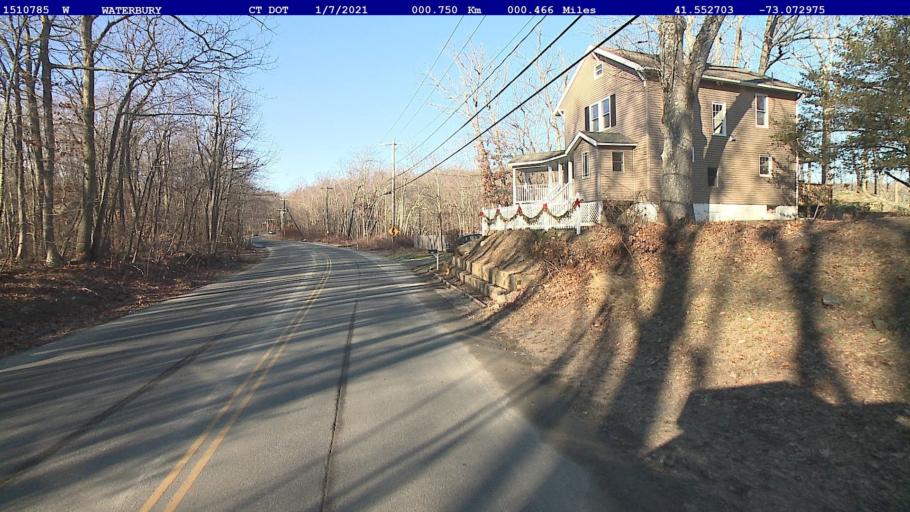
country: US
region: Connecticut
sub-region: New Haven County
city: Waterbury
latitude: 41.5527
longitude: -73.0730
